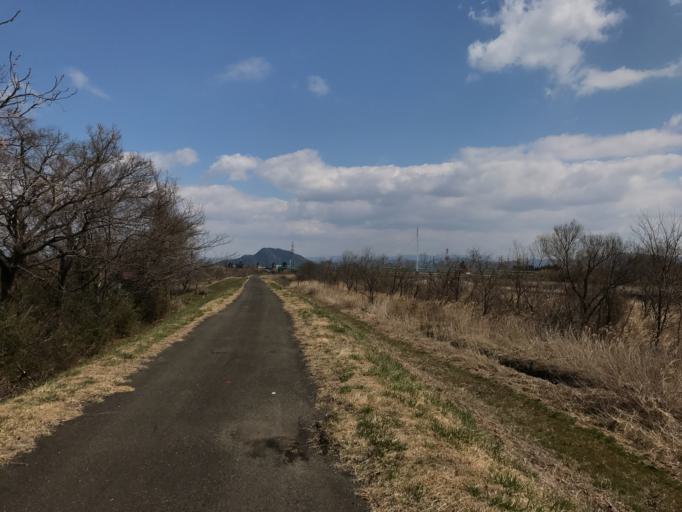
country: JP
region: Fukushima
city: Fukushima-shi
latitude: 37.7478
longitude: 140.4040
